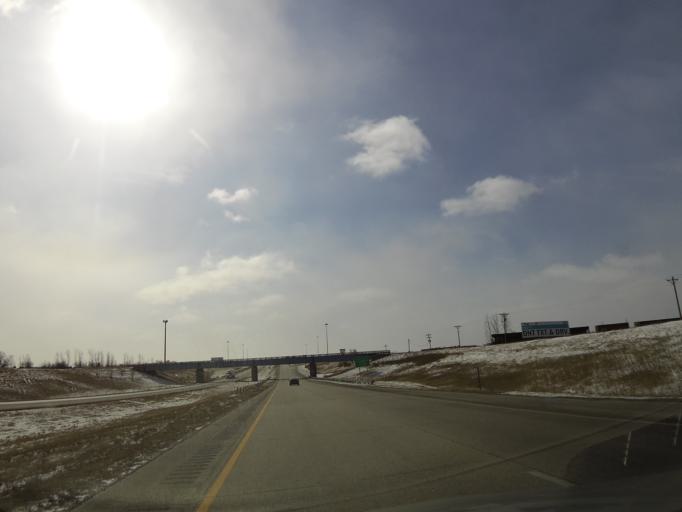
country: US
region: North Dakota
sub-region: Grand Forks County
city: Grand Forks
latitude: 47.9421
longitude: -97.0933
